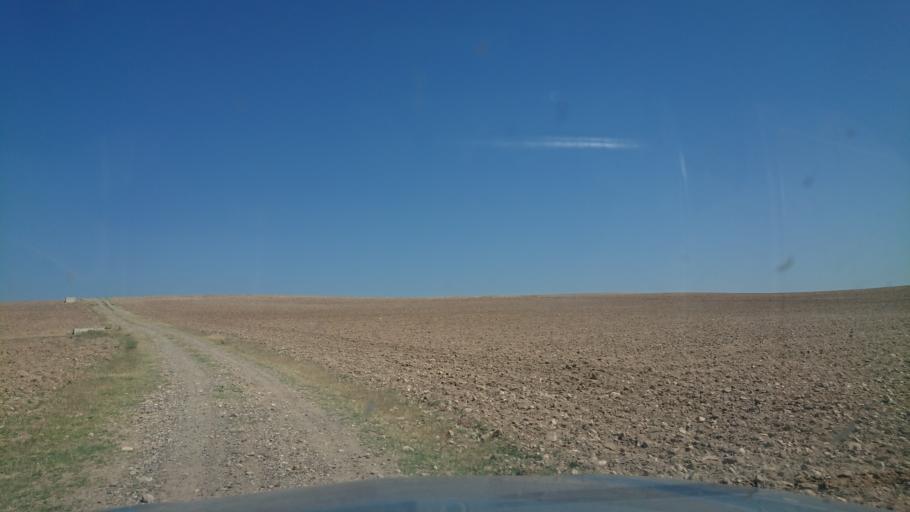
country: TR
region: Aksaray
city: Sariyahsi
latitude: 39.0536
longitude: 33.8893
